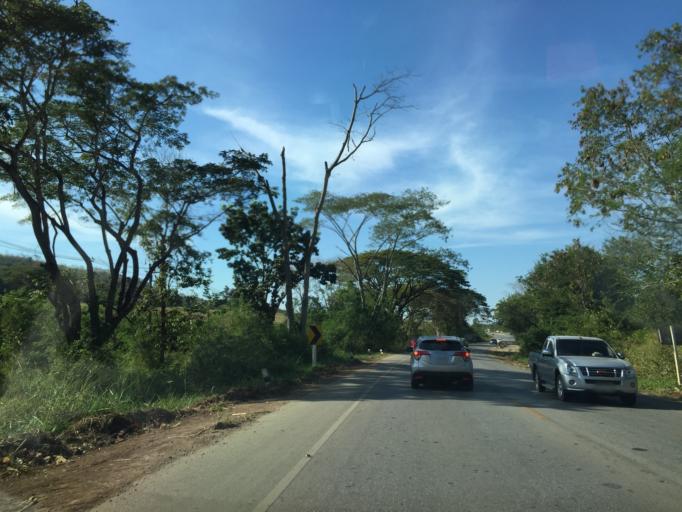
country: TH
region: Loei
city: Wang Saphung
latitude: 17.2907
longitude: 101.8225
